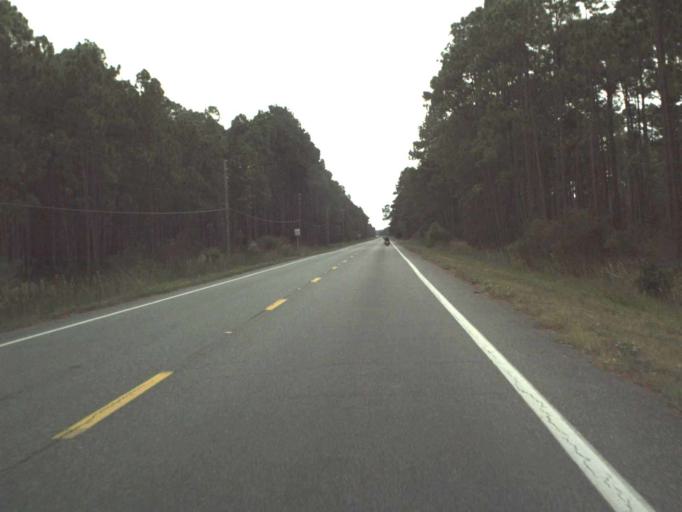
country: US
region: Florida
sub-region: Wakulla County
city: Crawfordville
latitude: 30.0438
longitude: -84.3879
